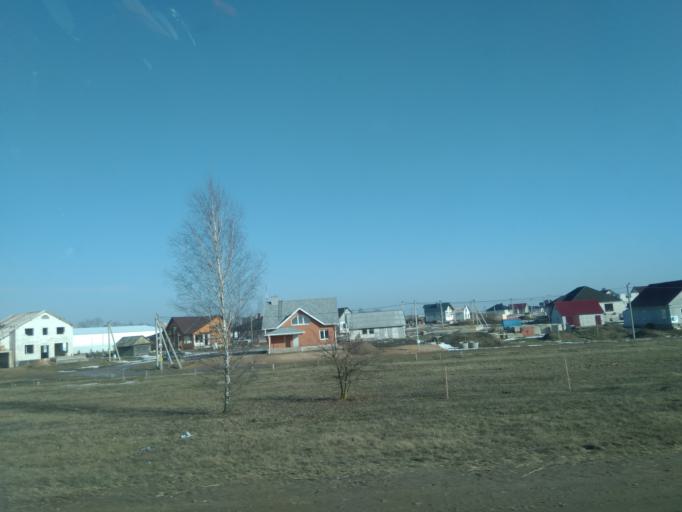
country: BY
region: Minsk
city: Nyasvizh
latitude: 53.2239
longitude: 26.6460
